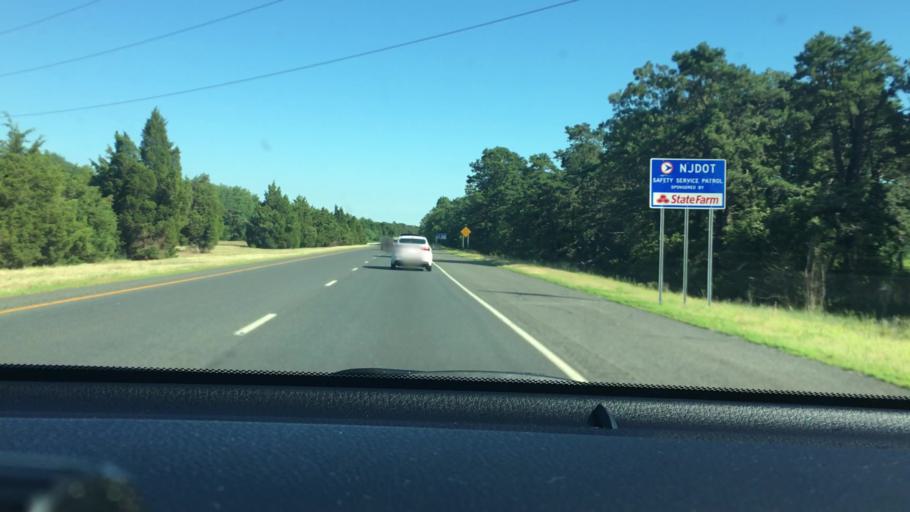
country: US
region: New Jersey
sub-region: Cumberland County
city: South Vineland
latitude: 39.4577
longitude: -75.0708
